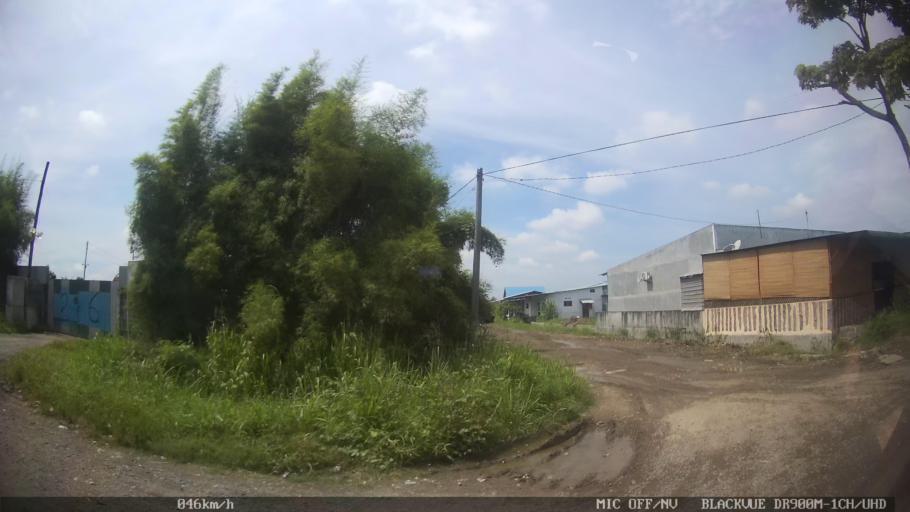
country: ID
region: North Sumatra
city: Medan
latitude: 3.6505
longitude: 98.7110
